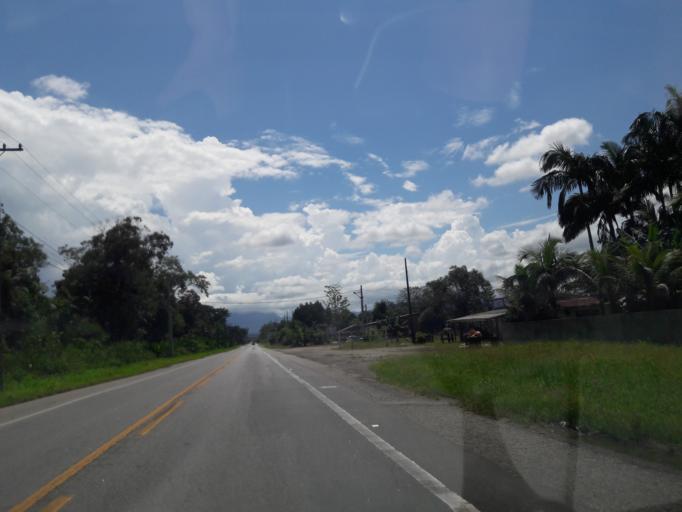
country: BR
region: Parana
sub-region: Antonina
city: Antonina
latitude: -25.5056
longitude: -48.8144
